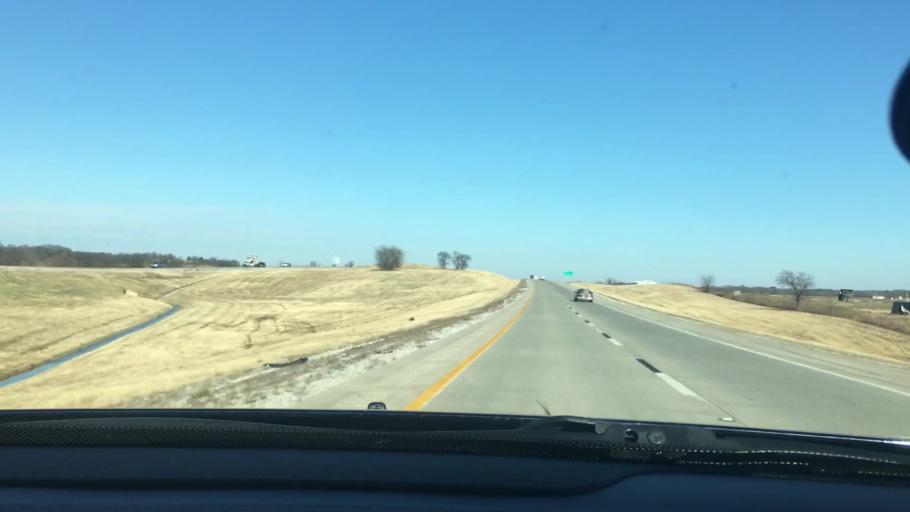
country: US
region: Oklahoma
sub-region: Carter County
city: Ardmore
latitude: 34.0804
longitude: -97.1495
